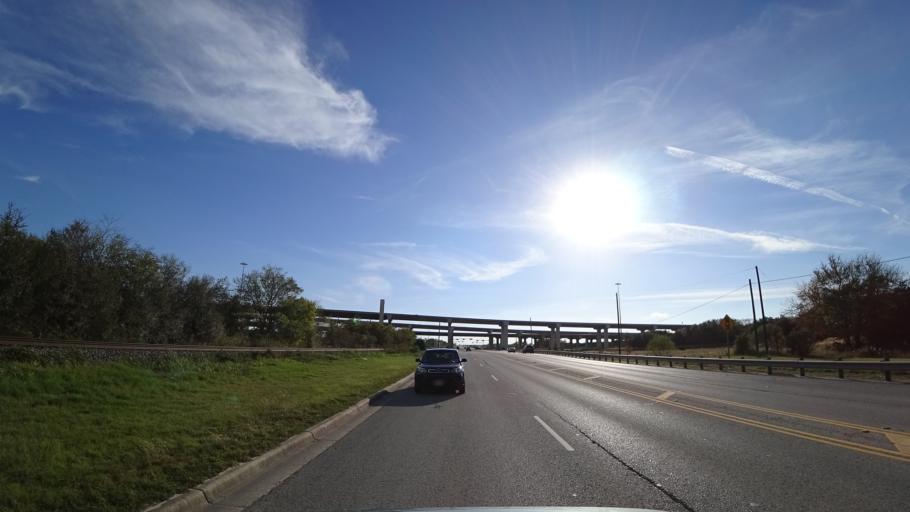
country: US
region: Texas
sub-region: Williamson County
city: Round Rock
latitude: 30.4790
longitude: -97.7043
